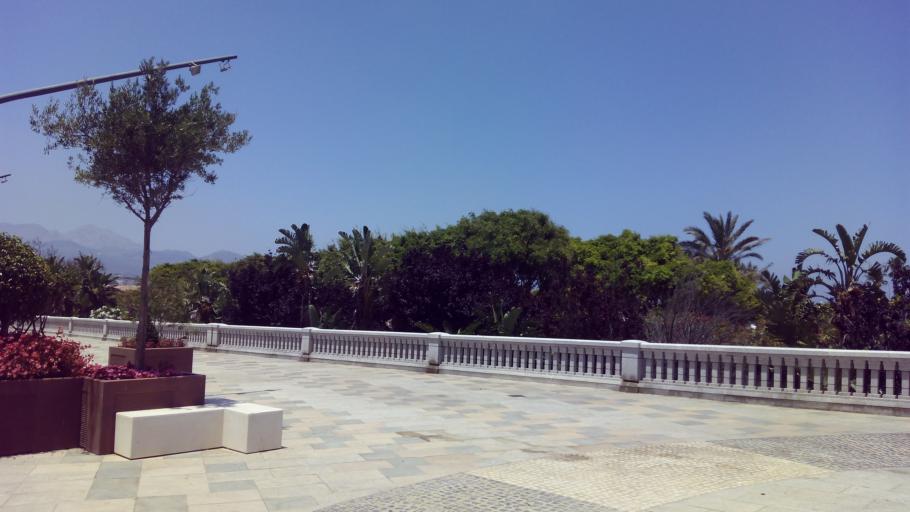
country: ES
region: Ceuta
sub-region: Ceuta
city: Ceuta
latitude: 35.8888
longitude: -5.3103
